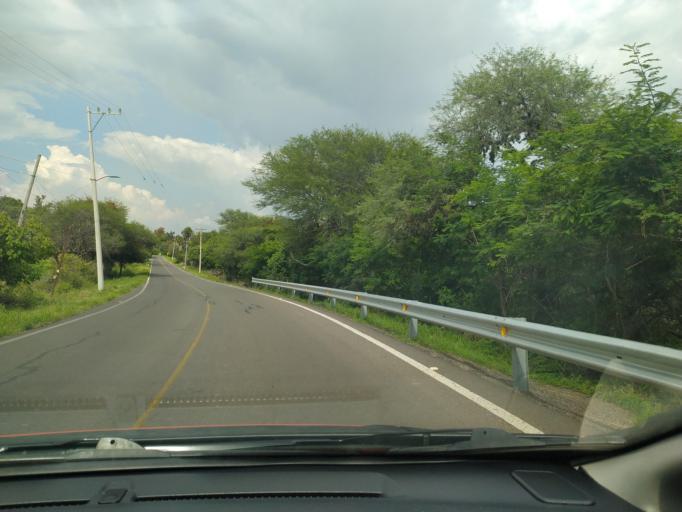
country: MX
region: Jalisco
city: Villa Corona
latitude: 20.4087
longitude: -103.6828
